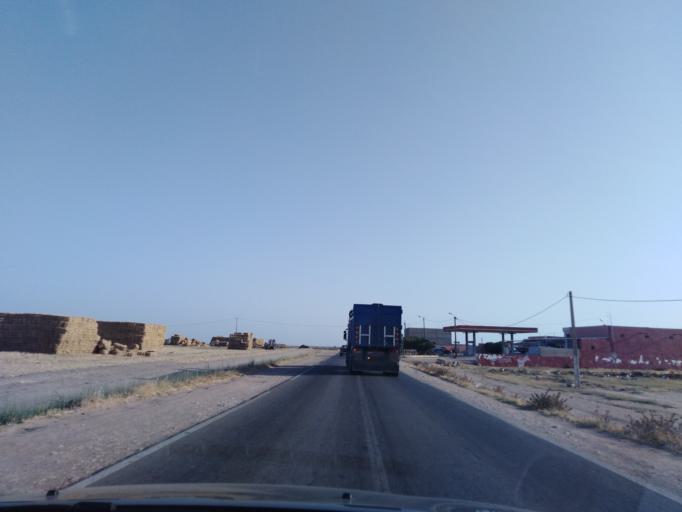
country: MA
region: Doukkala-Abda
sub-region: El-Jadida
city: Sidi Bennour
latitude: 32.5411
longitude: -8.7280
